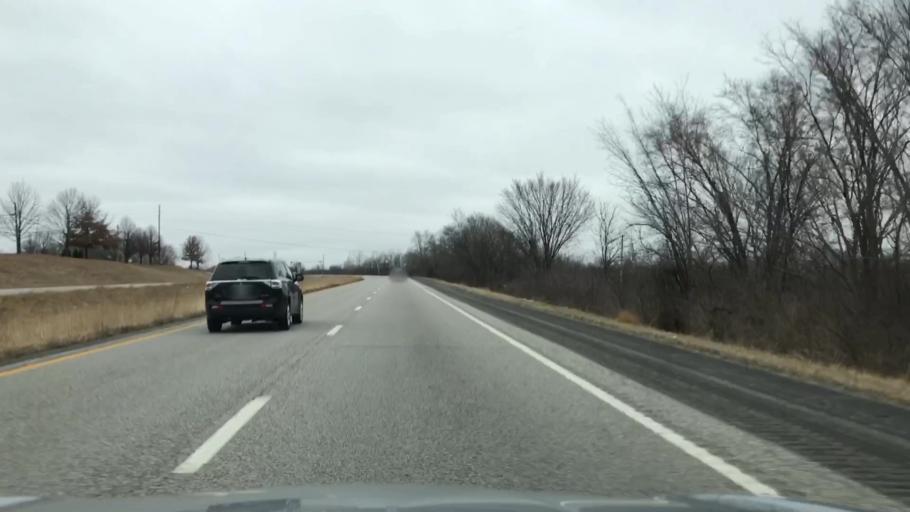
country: US
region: Missouri
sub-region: Clay County
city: Liberty
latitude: 39.2271
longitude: -94.4121
